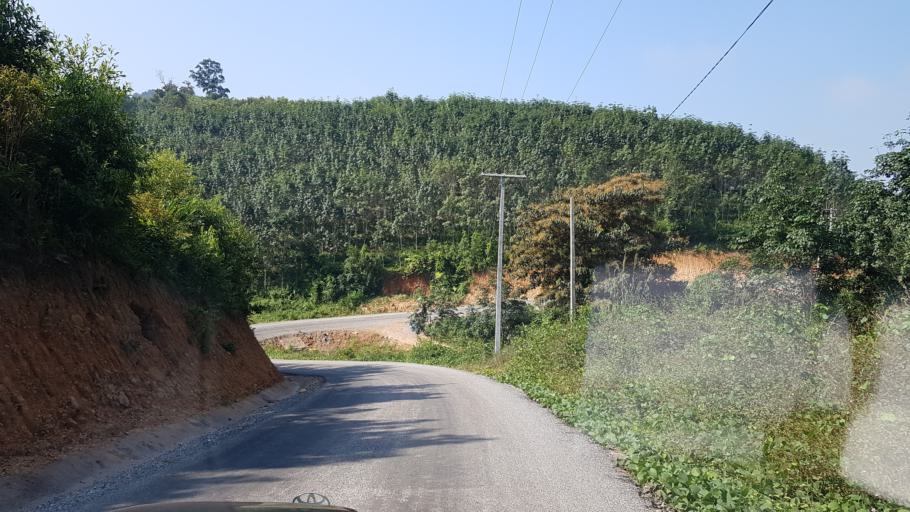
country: LA
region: Oudomxai
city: Muang Xay
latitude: 20.7150
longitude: 102.0764
